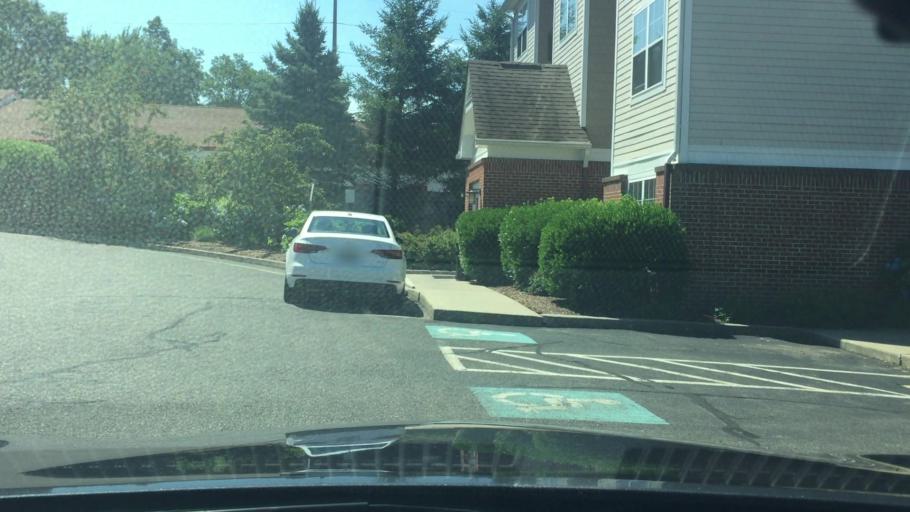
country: US
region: Connecticut
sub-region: New Haven County
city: City of Milford (balance)
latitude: 41.2114
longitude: -73.0917
